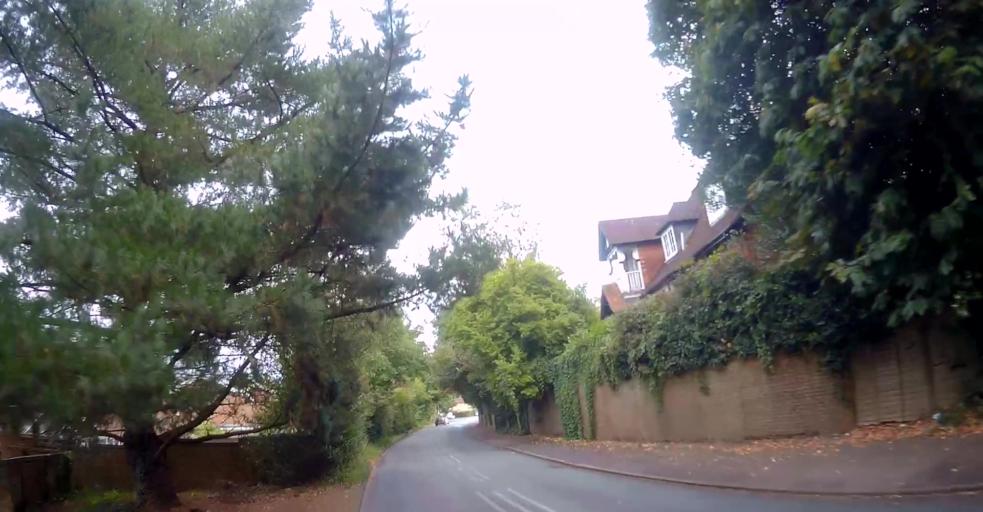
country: GB
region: England
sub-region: Surrey
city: Woking
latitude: 51.3133
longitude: -0.5784
